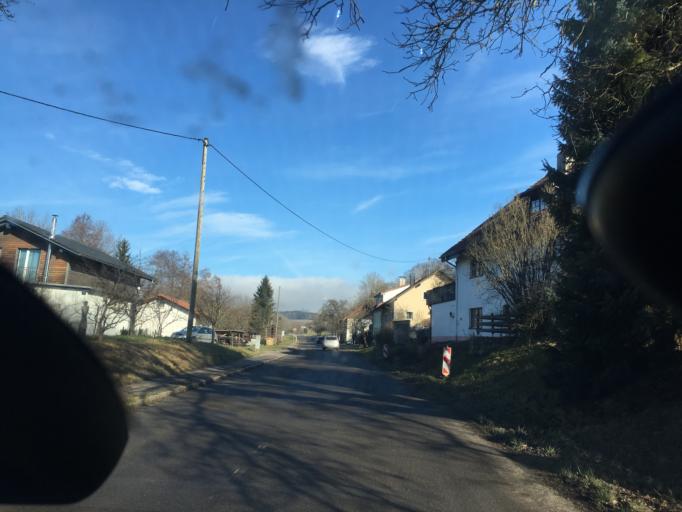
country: DE
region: Baden-Wuerttemberg
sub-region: Freiburg Region
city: Dogern
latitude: 47.6455
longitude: 8.1358
